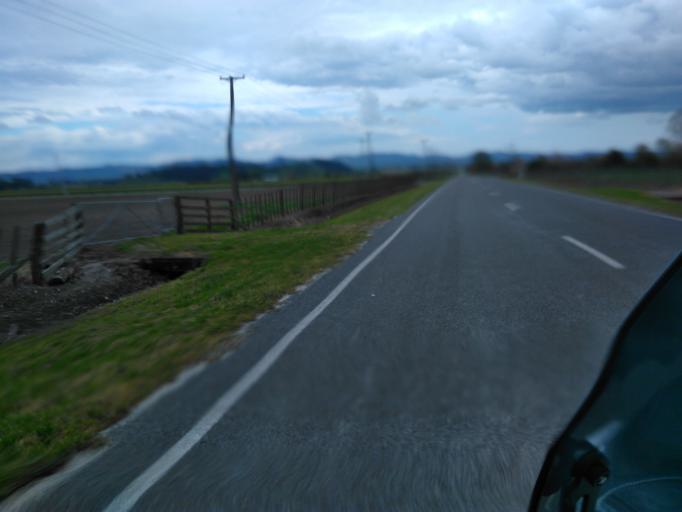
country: NZ
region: Gisborne
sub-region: Gisborne District
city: Gisborne
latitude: -38.6454
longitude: 177.8577
